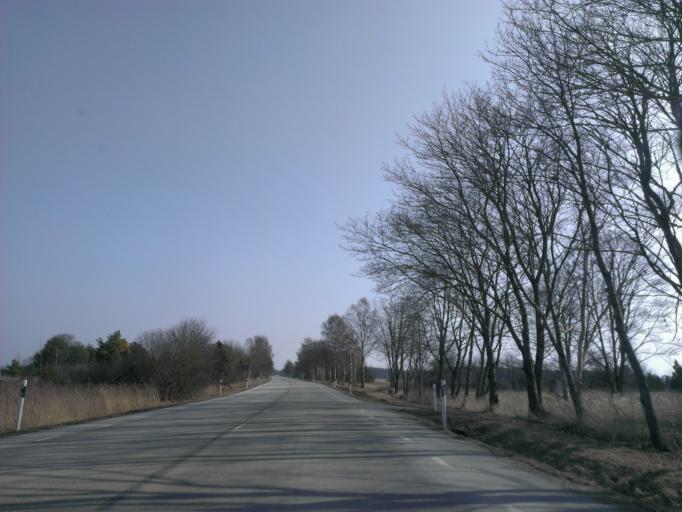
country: EE
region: Saare
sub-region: Orissaare vald
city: Orissaare
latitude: 58.5563
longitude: 23.0960
